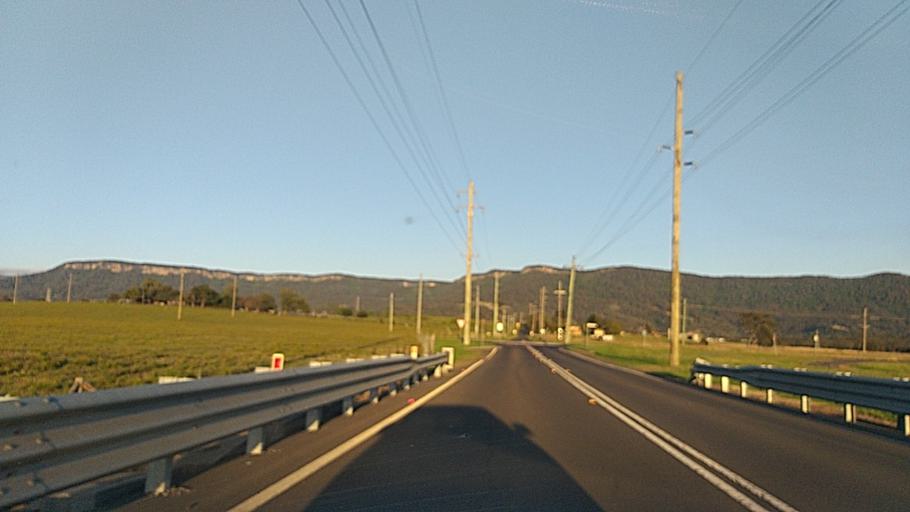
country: AU
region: New South Wales
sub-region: Wollongong
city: Dapto
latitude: -34.5027
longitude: 150.7796
